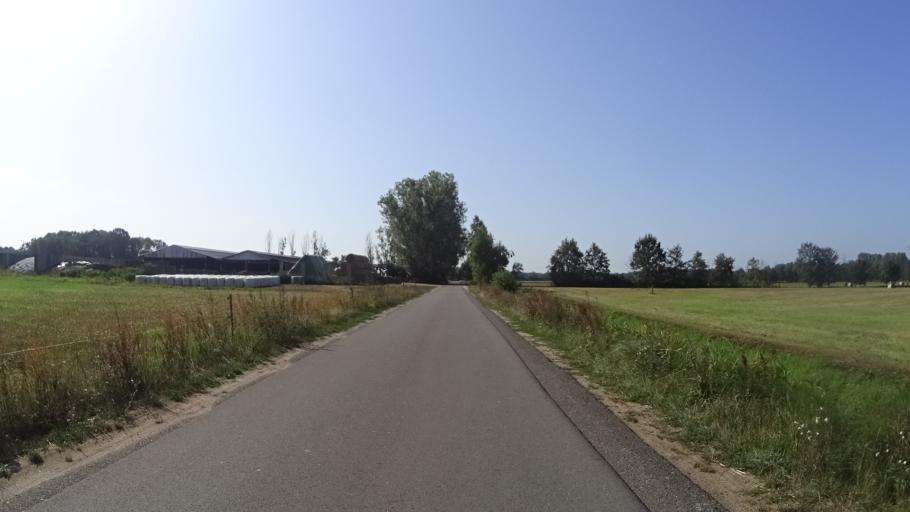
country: DE
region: Brandenburg
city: Straupitz
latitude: 51.8912
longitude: 14.1252
